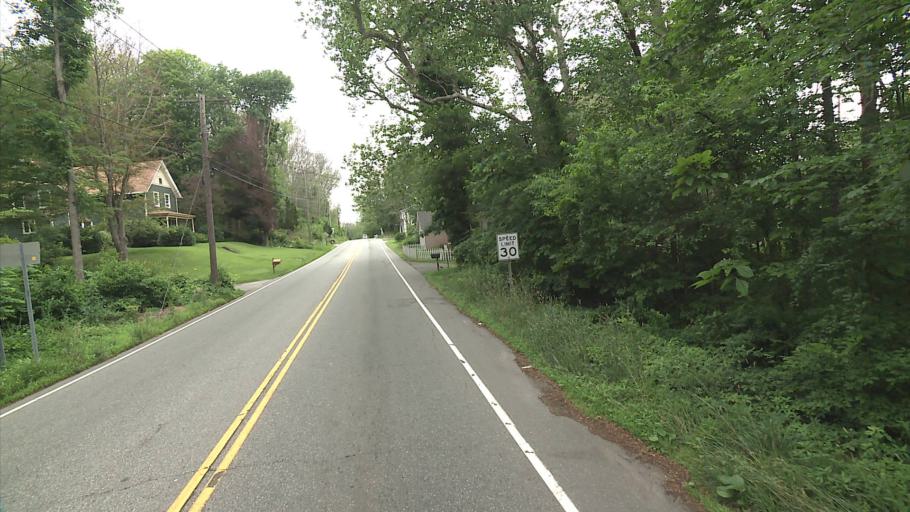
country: US
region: Connecticut
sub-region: New London County
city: Ledyard Center
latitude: 41.4885
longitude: -72.0346
